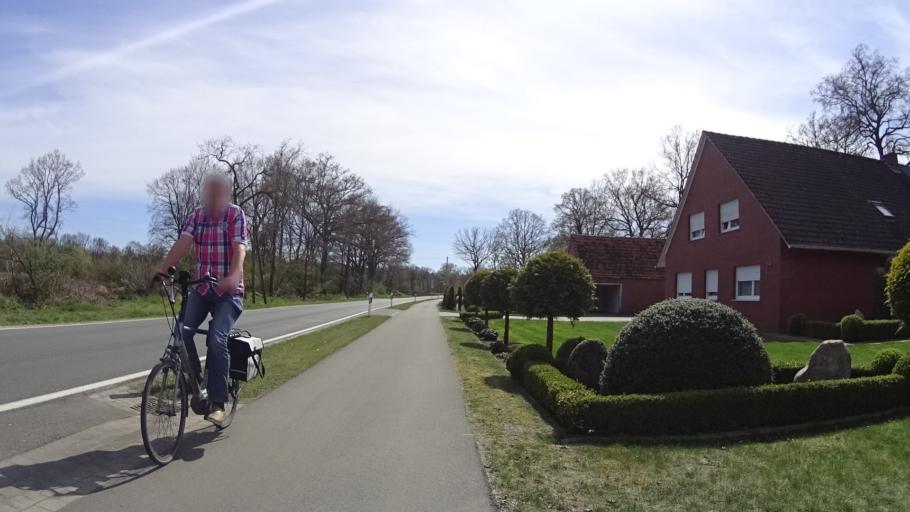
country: DE
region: Lower Saxony
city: Spelle
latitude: 52.3336
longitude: 7.4536
